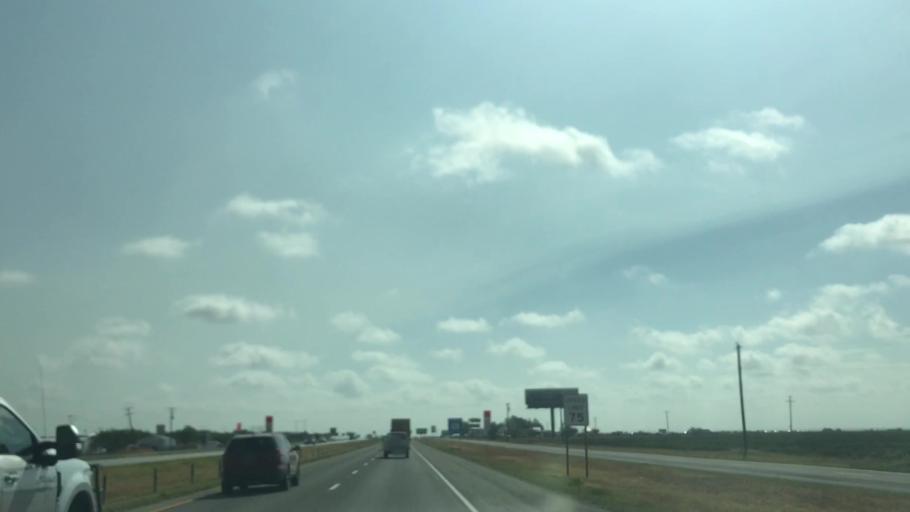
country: US
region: Texas
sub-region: Nolan County
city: Roscoe
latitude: 32.4495
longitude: -100.4886
